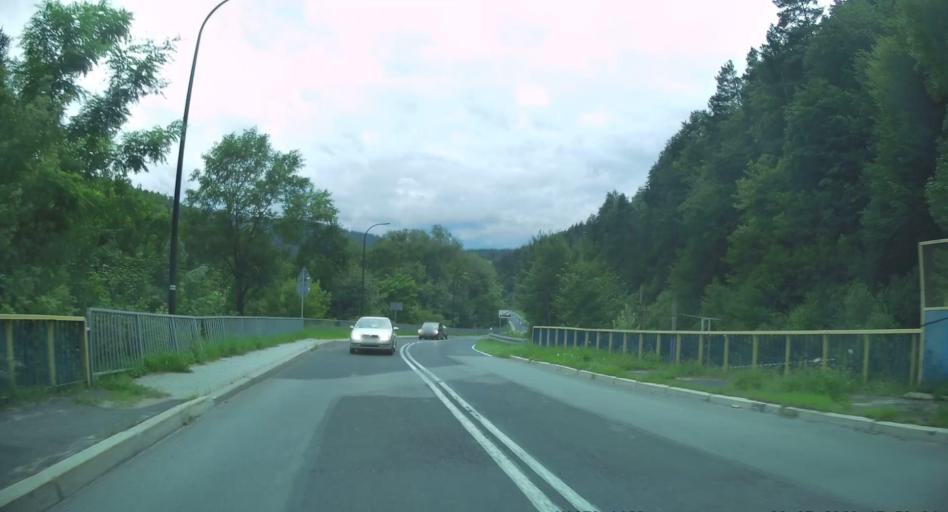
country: PL
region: Lesser Poland Voivodeship
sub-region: Powiat nowosadecki
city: Muszyna
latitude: 49.3634
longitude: 20.8019
